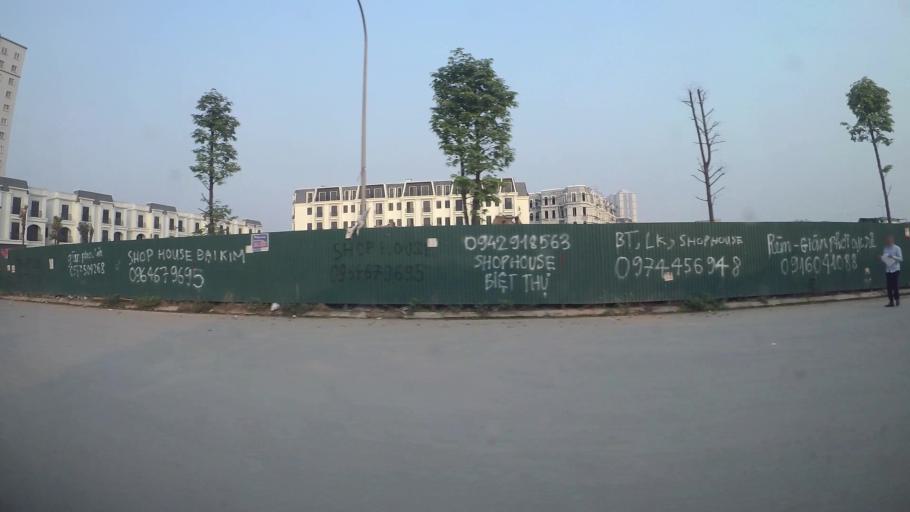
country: VN
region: Ha Noi
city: Thanh Xuan
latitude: 20.9799
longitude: 105.8130
